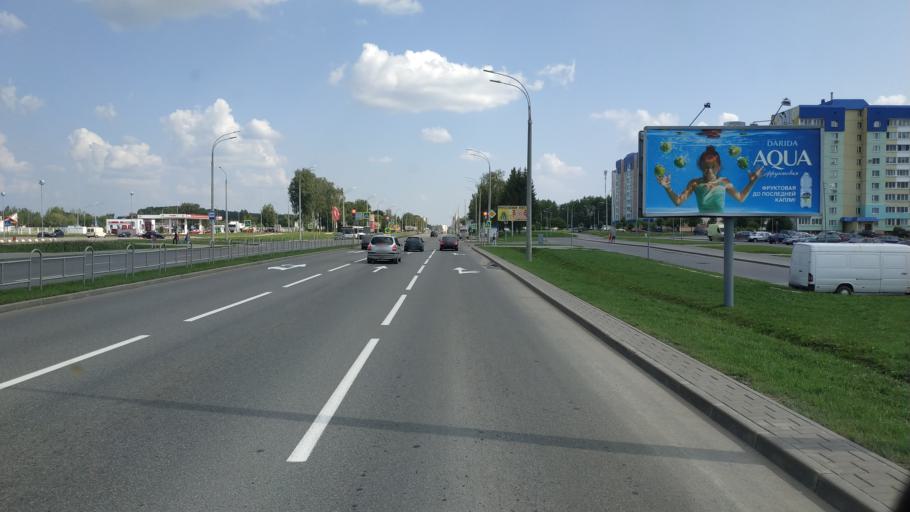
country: BY
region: Mogilev
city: Buynichy
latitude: 53.9343
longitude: 30.2547
